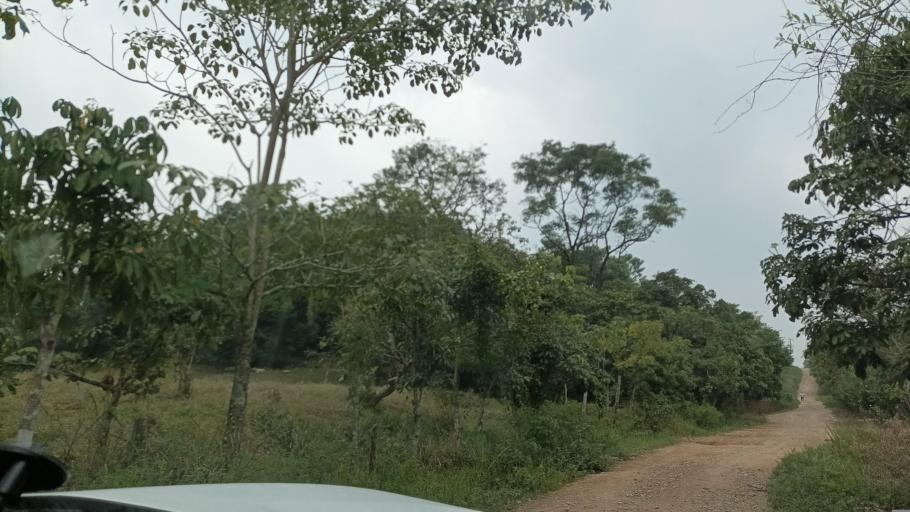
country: MX
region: Veracruz
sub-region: Moloacan
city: Cuichapa
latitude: 17.5753
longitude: -94.2281
